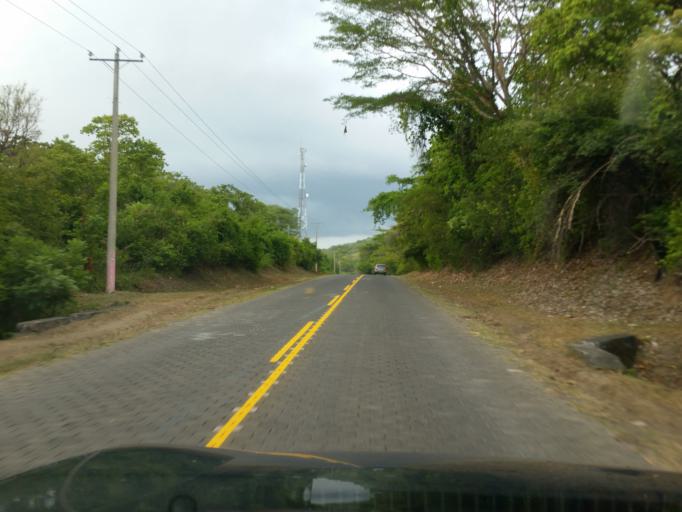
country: NI
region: Managua
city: Masachapa
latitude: 11.8563
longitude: -86.5185
